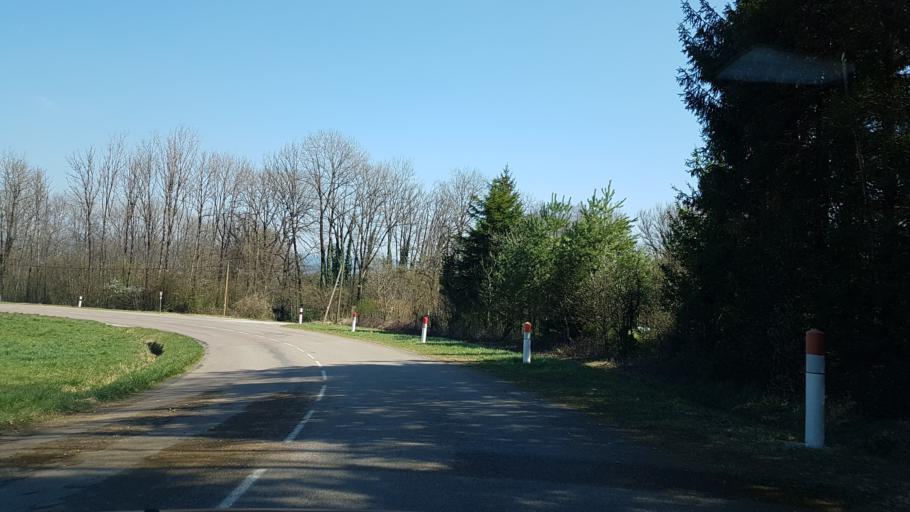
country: FR
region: Franche-Comte
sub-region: Departement du Jura
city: Orgelet
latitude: 46.5566
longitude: 5.6599
